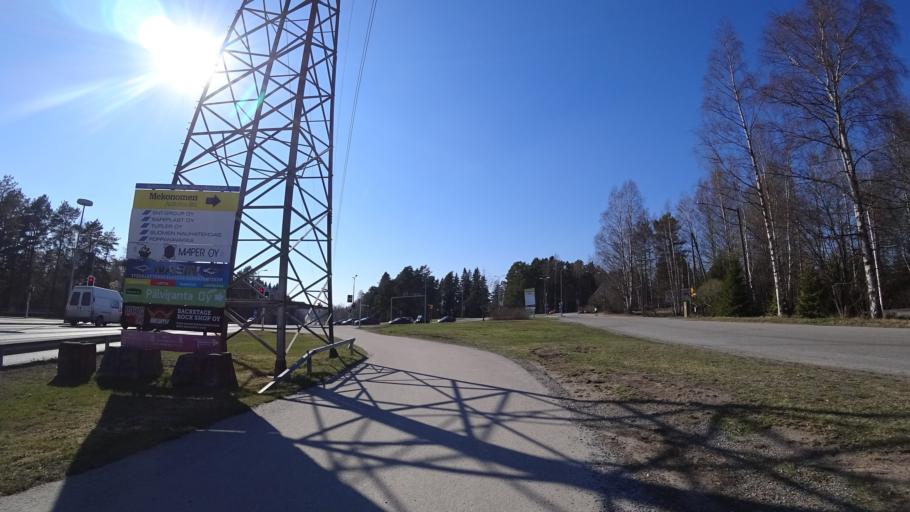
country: FI
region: Pirkanmaa
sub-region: Tampere
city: Pirkkala
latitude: 61.5194
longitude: 23.6445
